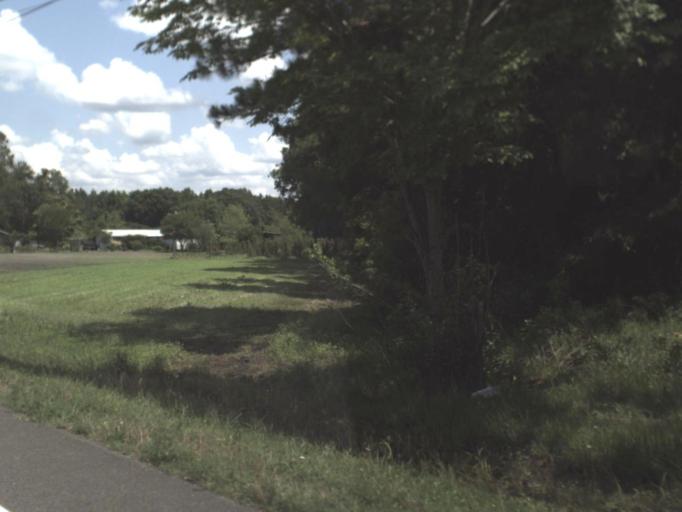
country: US
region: Florida
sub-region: Nassau County
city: Nassau Village-Ratliff
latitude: 30.4780
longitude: -81.7147
